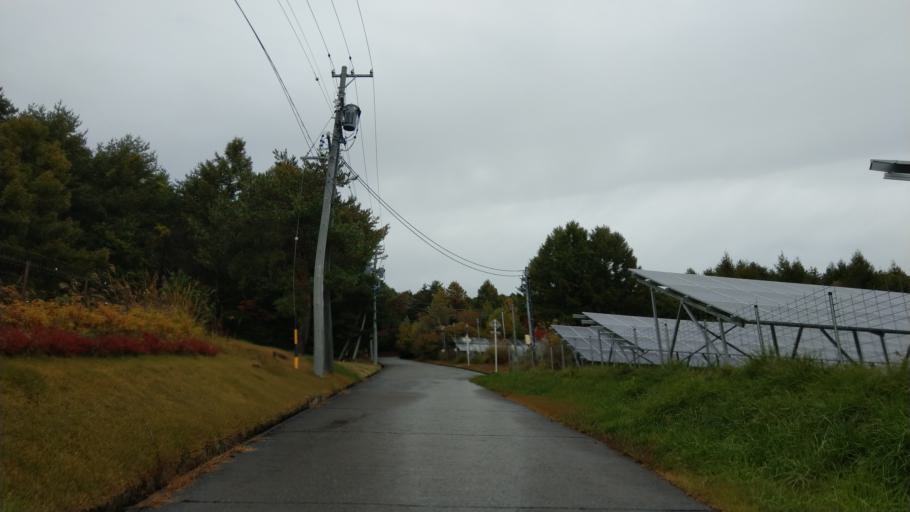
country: JP
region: Nagano
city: Komoro
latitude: 36.3644
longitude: 138.4264
